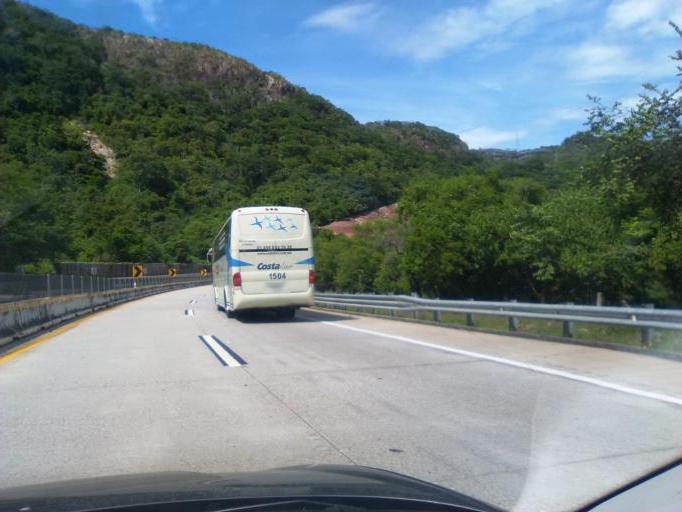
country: MX
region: Guerrero
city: Tierra Colorada
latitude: 17.1205
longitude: -99.5688
